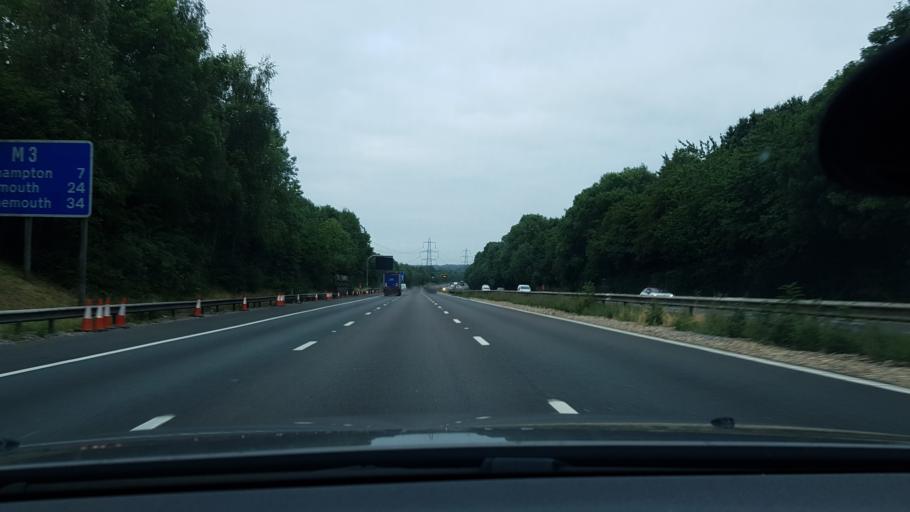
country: GB
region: England
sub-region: Hampshire
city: Eastleigh
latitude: 50.9878
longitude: -1.3624
